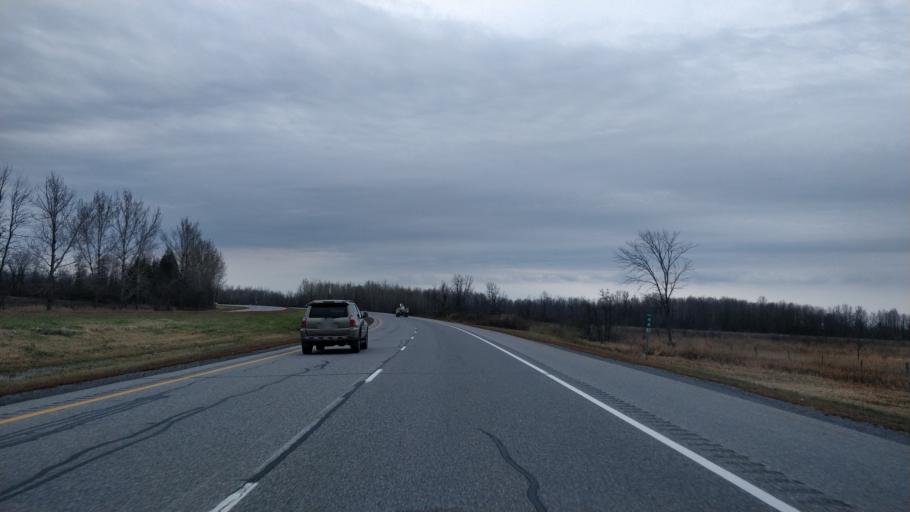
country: CA
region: Ontario
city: Bells Corners
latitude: 45.1214
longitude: -75.6760
